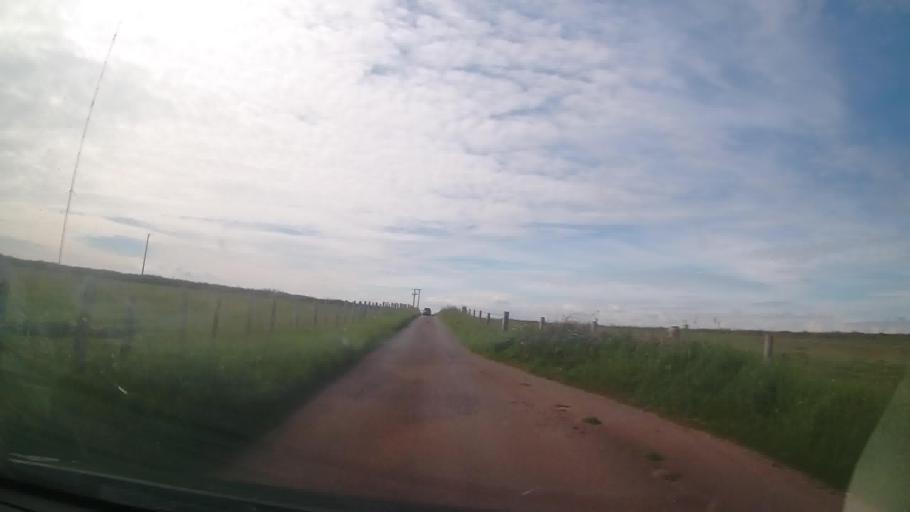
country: GB
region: England
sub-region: Devon
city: Salcombe
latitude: 50.2282
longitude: -3.6602
